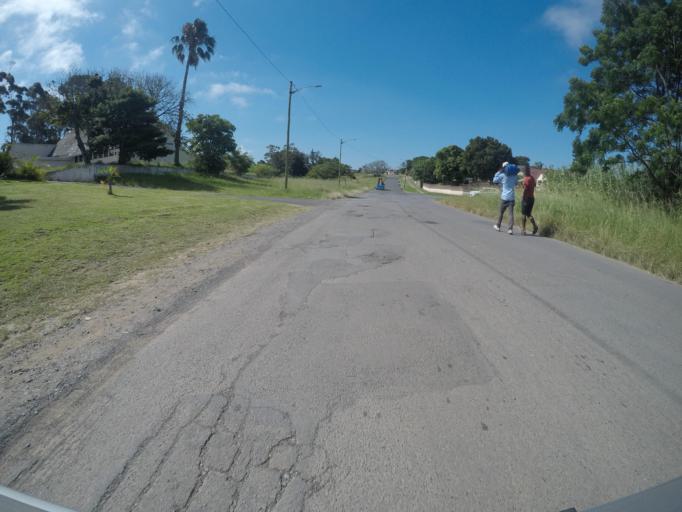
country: ZA
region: Eastern Cape
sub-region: Buffalo City Metropolitan Municipality
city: East London
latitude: -32.9838
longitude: 27.8853
